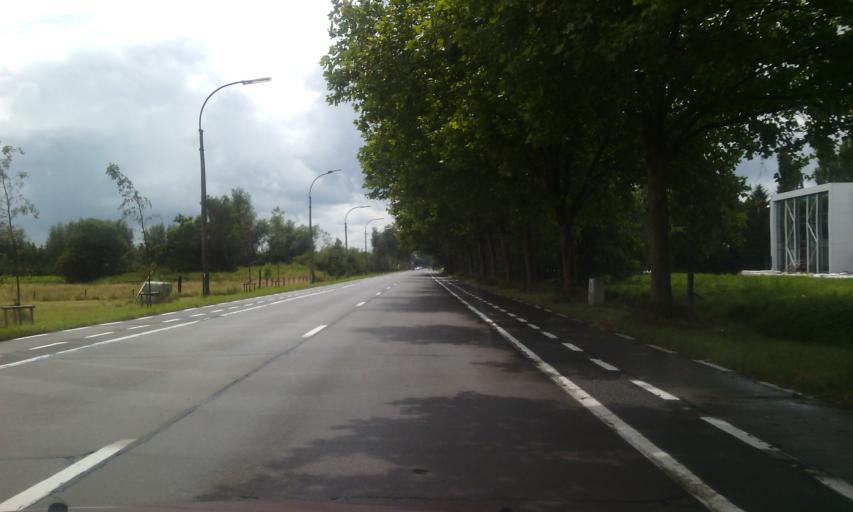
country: BE
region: Flanders
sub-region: Provincie Oost-Vlaanderen
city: Wetteren
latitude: 51.0216
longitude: 3.8857
